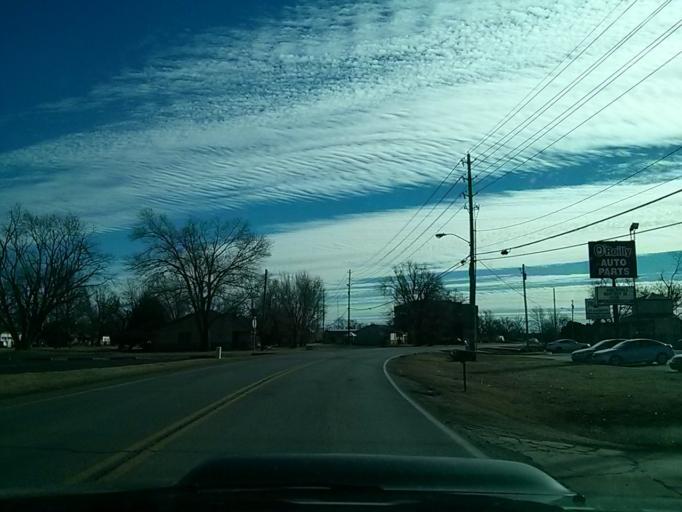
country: US
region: Oklahoma
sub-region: Tulsa County
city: Jenks
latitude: 36.0241
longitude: -95.9821
